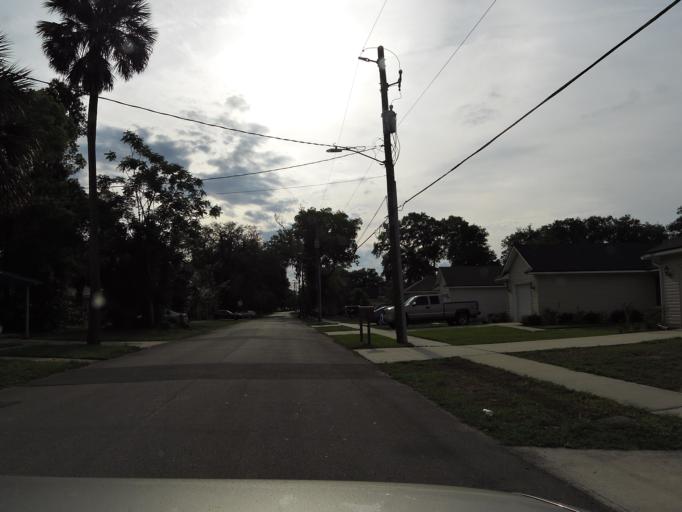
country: US
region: Florida
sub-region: Duval County
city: Jacksonville
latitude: 30.3317
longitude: -81.5996
